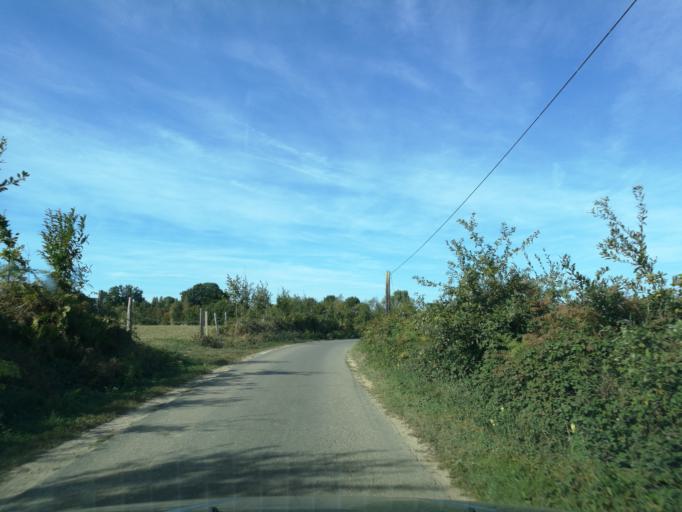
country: FR
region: Brittany
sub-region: Departement d'Ille-et-Vilaine
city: Pleumeleuc
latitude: 48.1985
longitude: -1.9220
